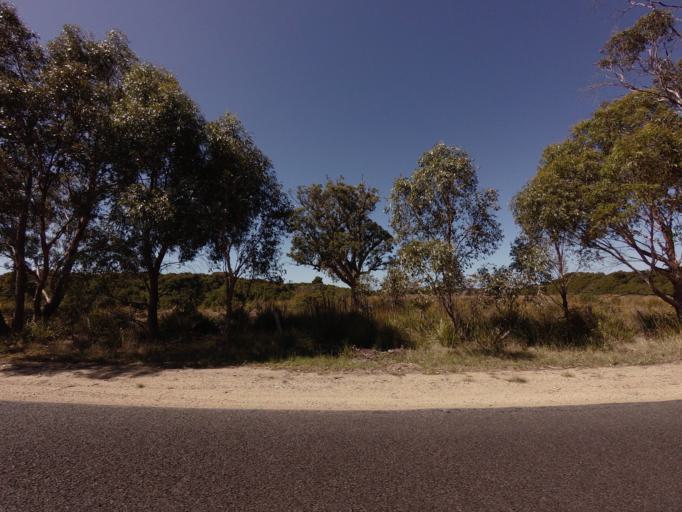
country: AU
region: Tasmania
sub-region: Break O'Day
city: St Helens
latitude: -41.7190
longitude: 148.2742
